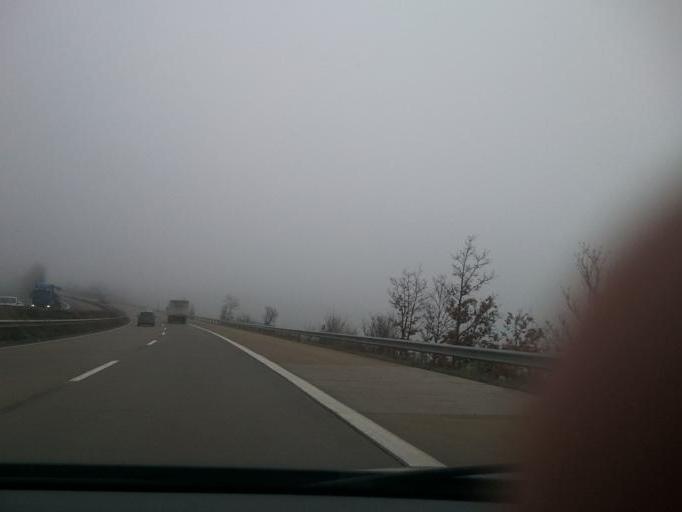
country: DE
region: Rheinland-Pfalz
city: Tiefenthal
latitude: 49.5331
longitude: 8.1045
